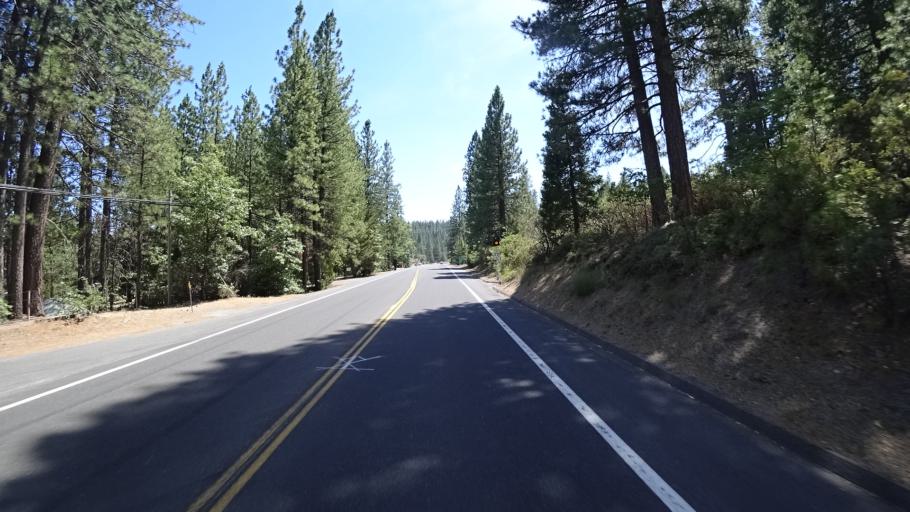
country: US
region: California
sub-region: Calaveras County
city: Arnold
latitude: 38.2077
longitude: -120.3685
